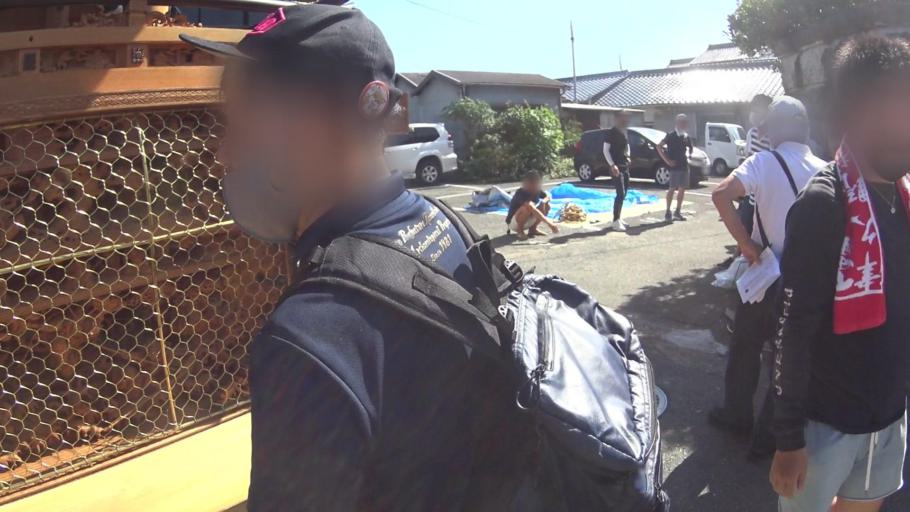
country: JP
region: Ehime
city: Kihoku-cho
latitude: 33.4038
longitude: 132.8752
